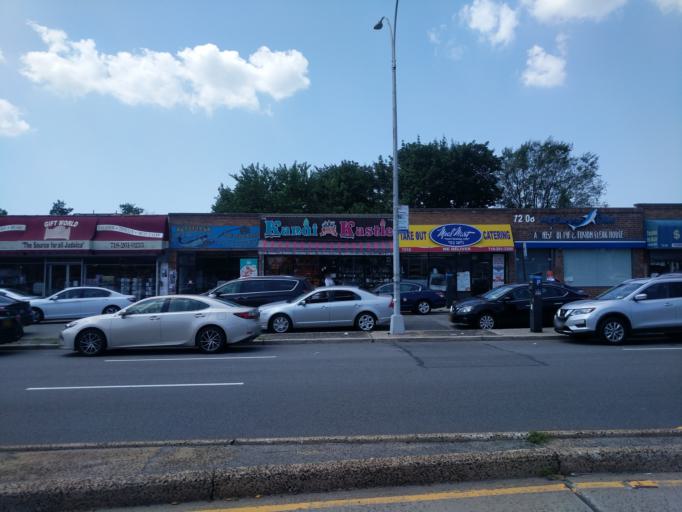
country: US
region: New York
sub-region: Queens County
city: Jamaica
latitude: 40.7263
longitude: -73.8217
